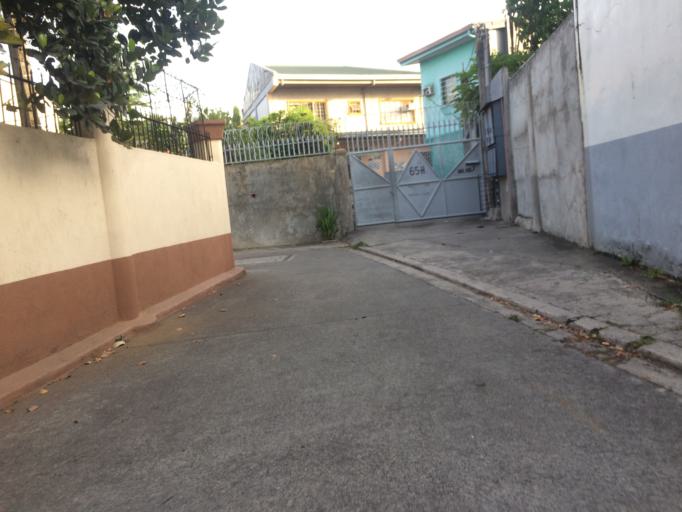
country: PH
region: Calabarzon
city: Bagong Pagasa
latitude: 14.6763
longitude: 121.0238
